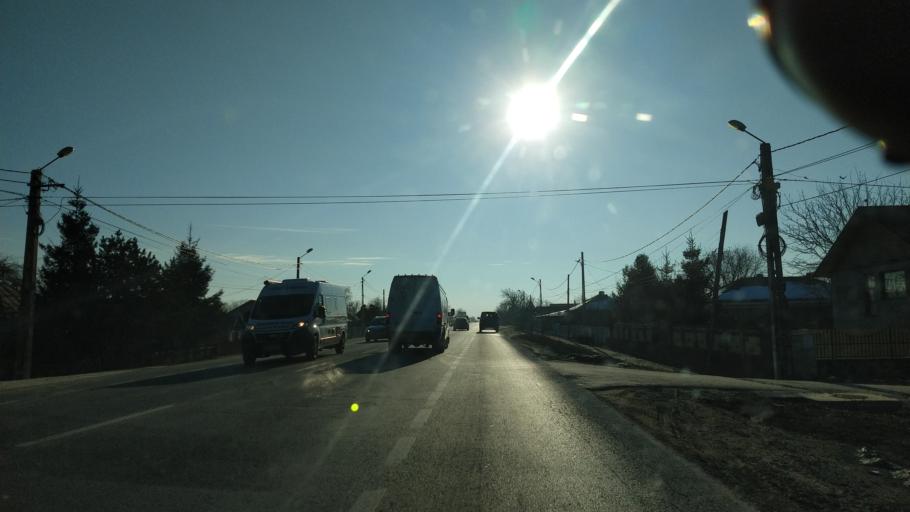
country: RO
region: Neamt
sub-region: Municipiul Roman
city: Roman
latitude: 46.9072
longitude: 26.9148
